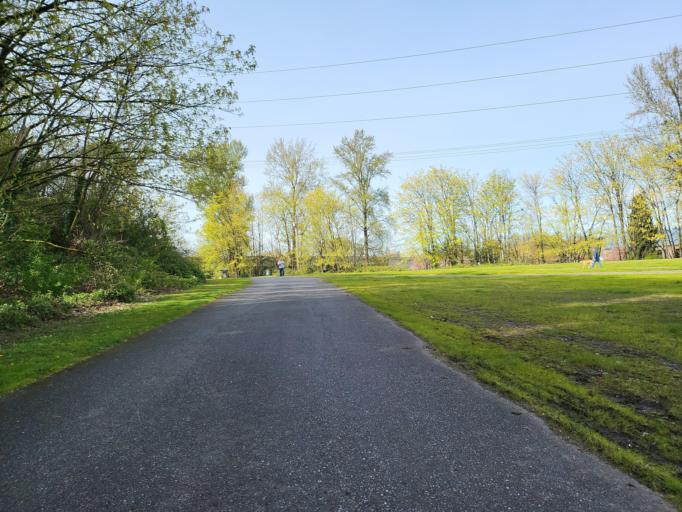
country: US
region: Washington
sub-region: King County
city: Renton
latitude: 47.4795
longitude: -122.1986
